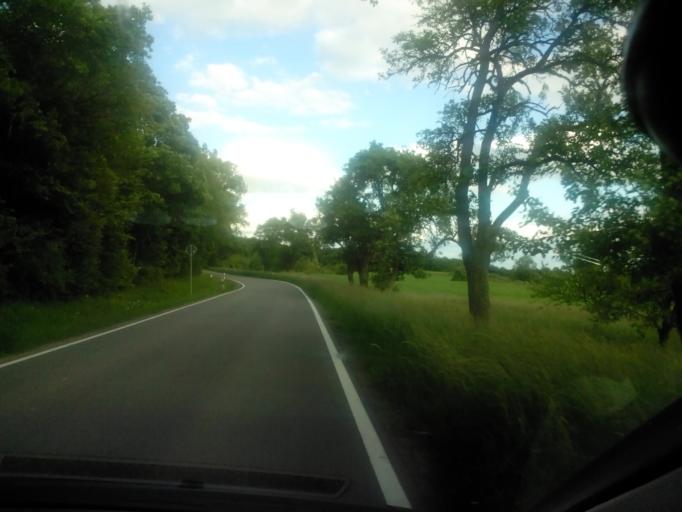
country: DE
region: Saarland
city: Rehlingen-Siersburg
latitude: 49.3783
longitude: 6.6202
